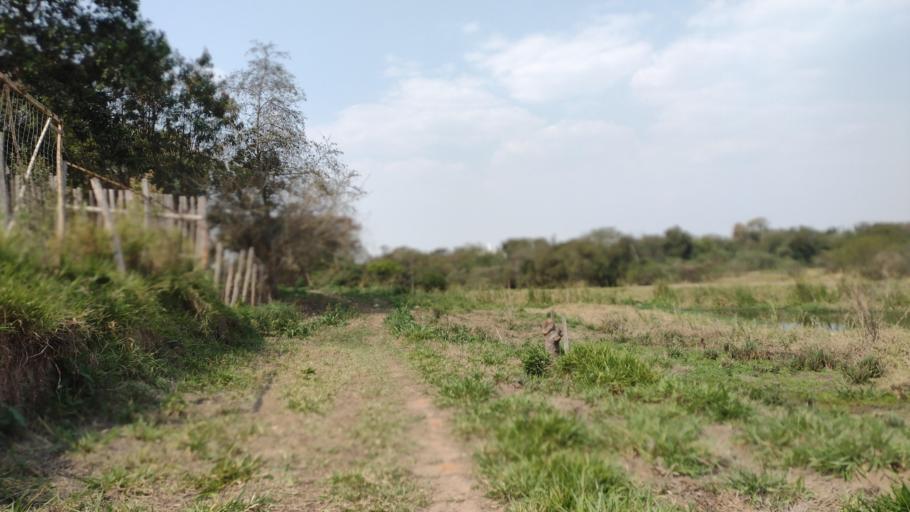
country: BR
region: Sao Paulo
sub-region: Sorocaba
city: Sorocaba
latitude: -23.4389
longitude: -47.4611
